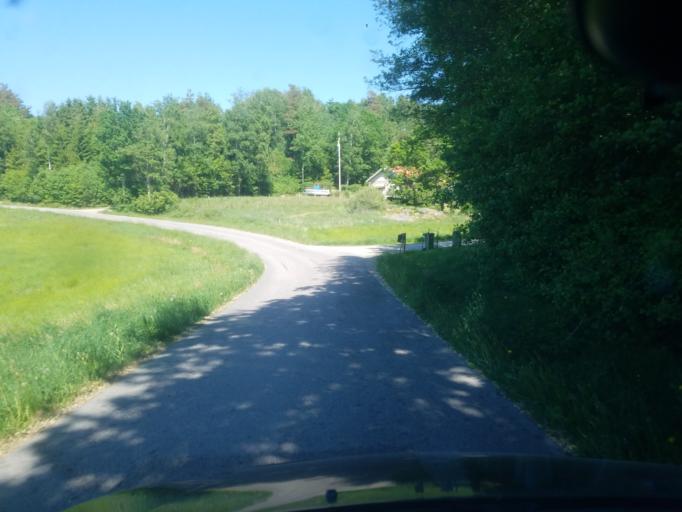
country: SE
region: Vaestra Goetaland
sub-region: Orust
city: Henan
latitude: 58.2760
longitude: 11.5769
